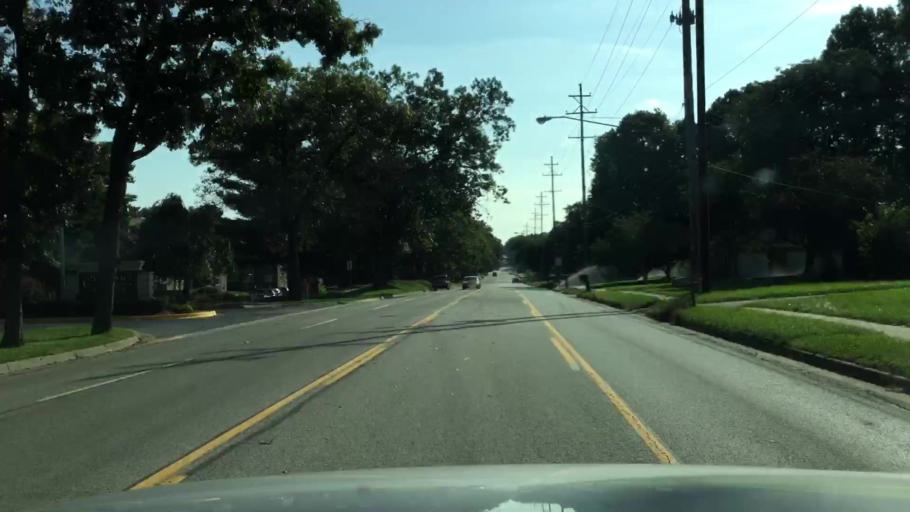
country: US
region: Michigan
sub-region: Kalamazoo County
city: Portage
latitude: 42.2450
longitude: -85.5837
